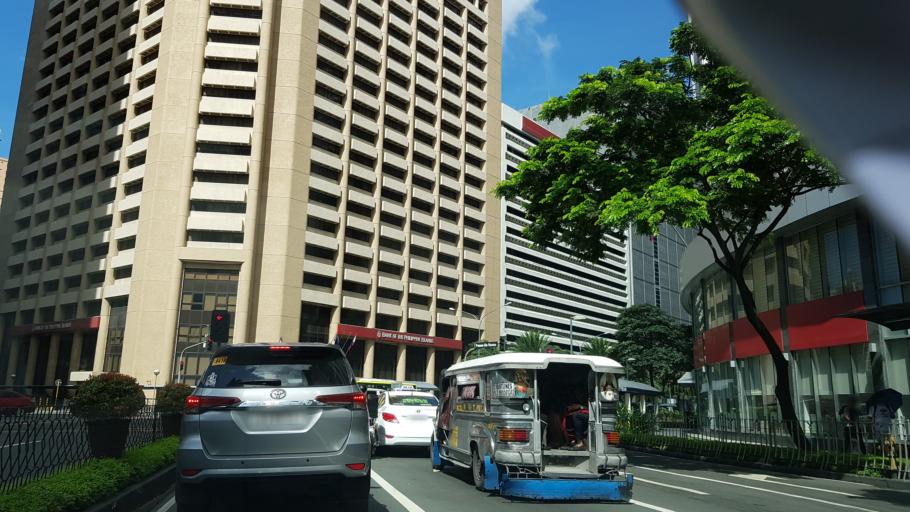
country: PH
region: Metro Manila
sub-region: Makati City
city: Makati City
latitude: 14.5575
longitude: 121.0227
